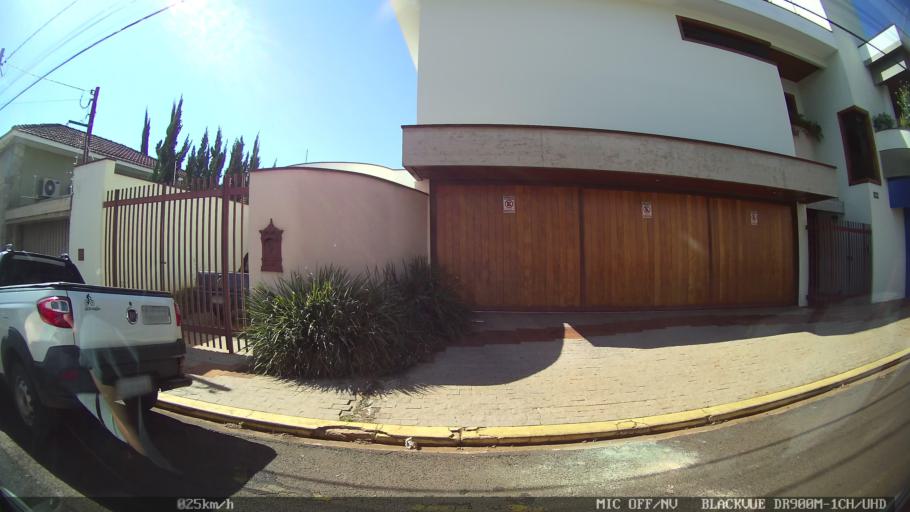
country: BR
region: Sao Paulo
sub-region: Batatais
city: Batatais
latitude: -20.8914
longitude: -47.5832
